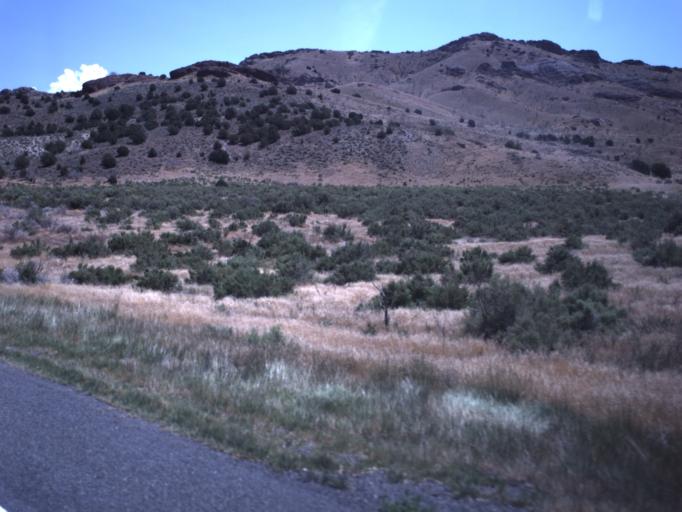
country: US
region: Utah
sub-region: Juab County
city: Nephi
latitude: 39.5765
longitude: -112.1819
